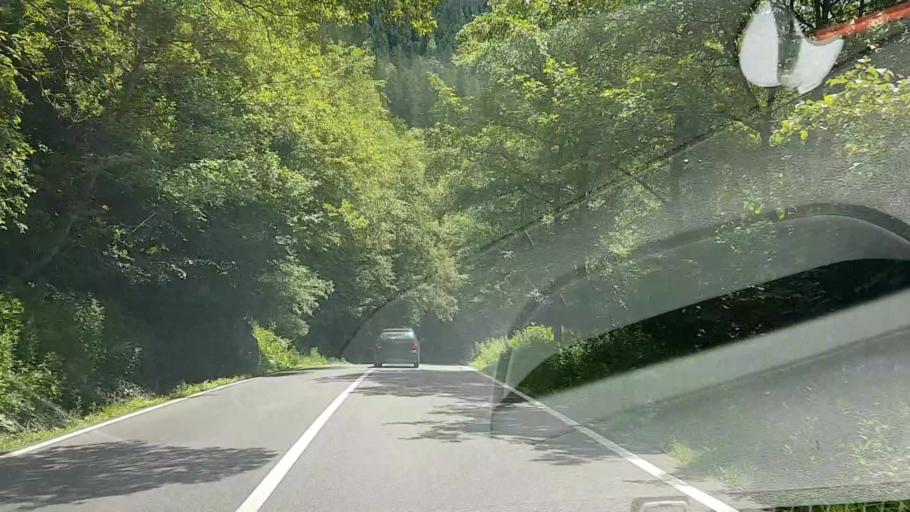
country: RO
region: Suceava
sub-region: Comuna Brosteni
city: Brosteni
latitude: 47.2821
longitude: 25.6486
